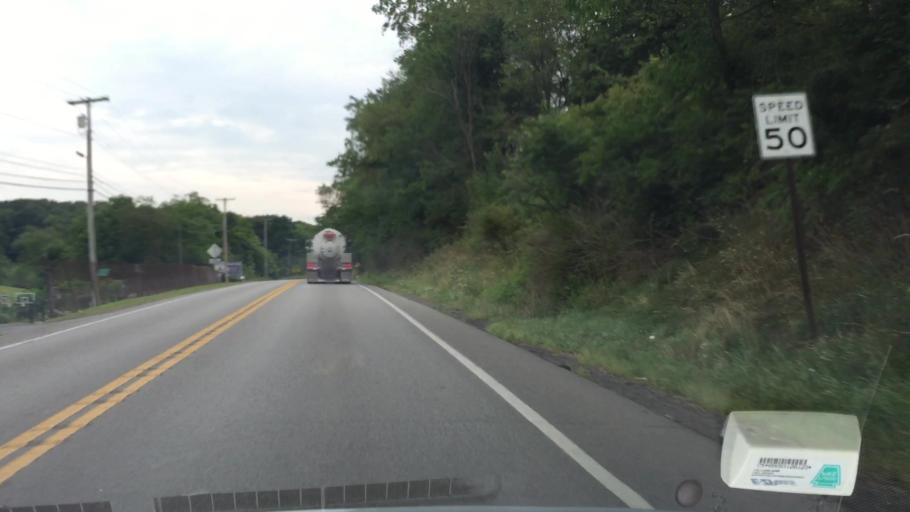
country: US
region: Pennsylvania
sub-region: Allegheny County
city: Bakerstown
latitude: 40.6991
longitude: -79.9459
